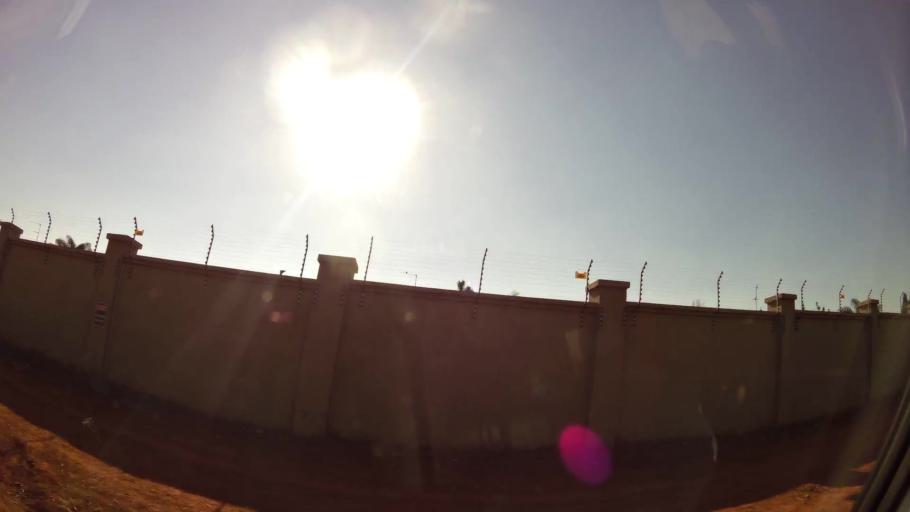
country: ZA
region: Gauteng
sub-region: City of Tshwane Metropolitan Municipality
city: Centurion
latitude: -25.8399
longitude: 28.2821
